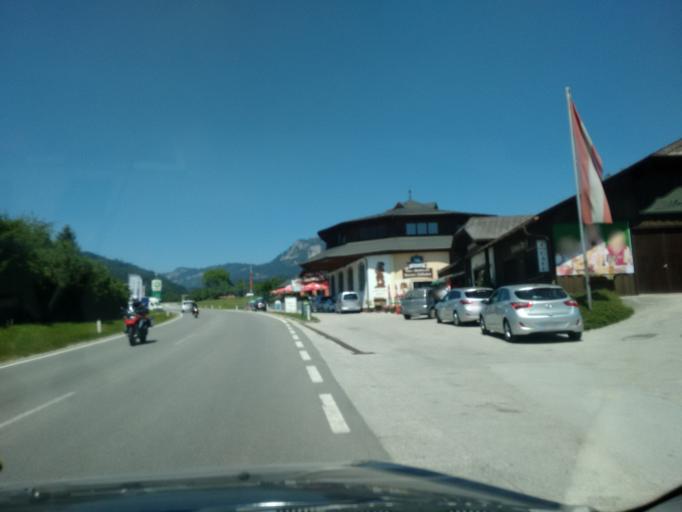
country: AT
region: Styria
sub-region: Politischer Bezirk Liezen
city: Bad Aussee
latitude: 47.6125
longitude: 13.7675
